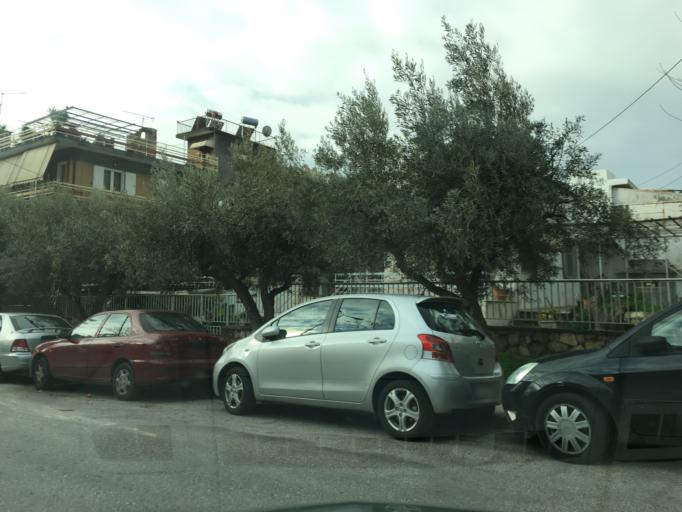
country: GR
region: Attica
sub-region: Nomarchia Athinas
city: Filothei
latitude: 38.0297
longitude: 23.7856
